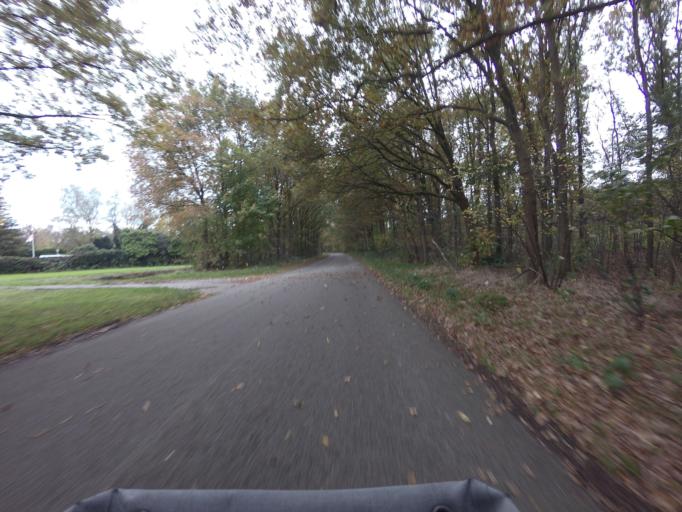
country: NL
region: North Holland
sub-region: Gemeente Laren
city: Laren
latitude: 52.2263
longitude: 5.2281
